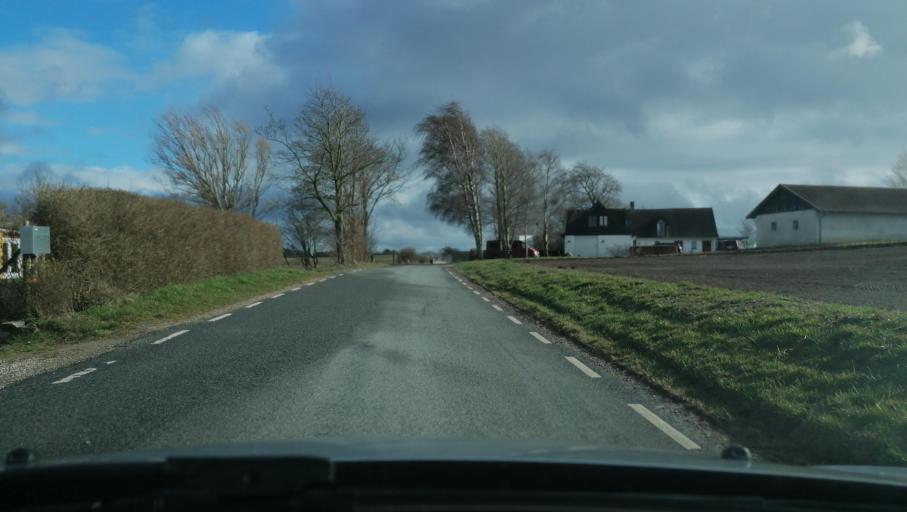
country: DK
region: Zealand
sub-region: Odsherred Kommune
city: Horve
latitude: 55.7500
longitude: 11.3971
